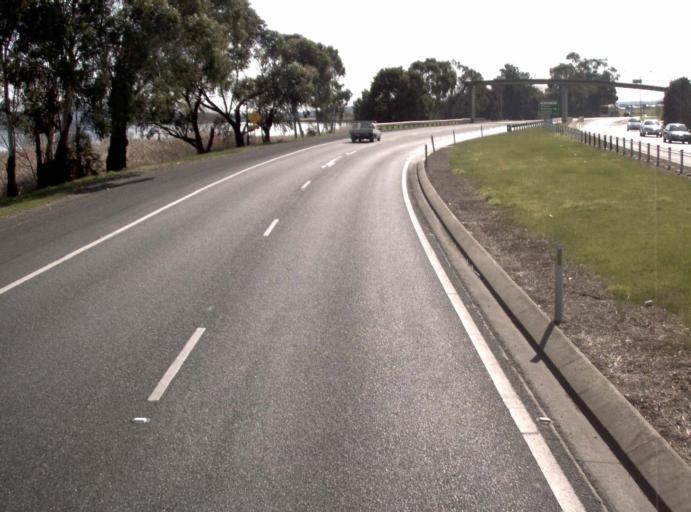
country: AU
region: Tasmania
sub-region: Launceston
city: Newnham
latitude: -41.4013
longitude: 147.1173
